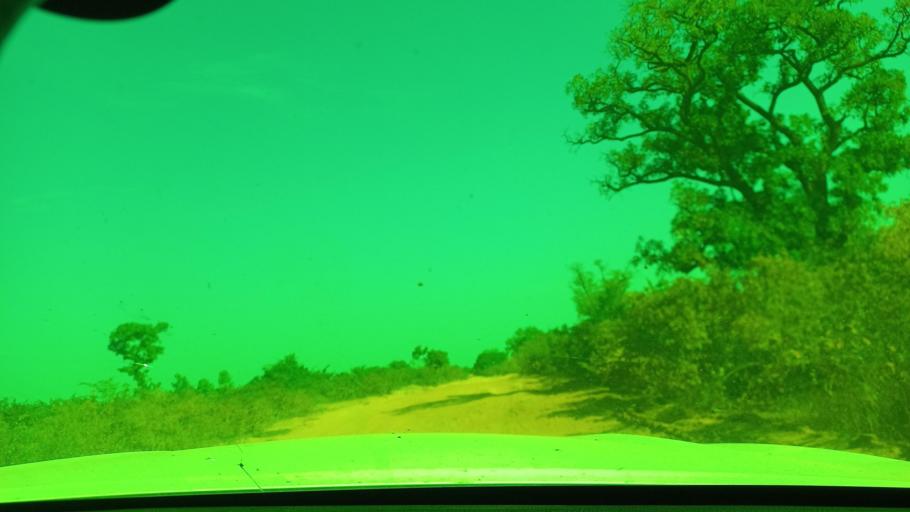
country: ML
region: Bamako
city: Bamako
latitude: 12.3965
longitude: -7.9819
